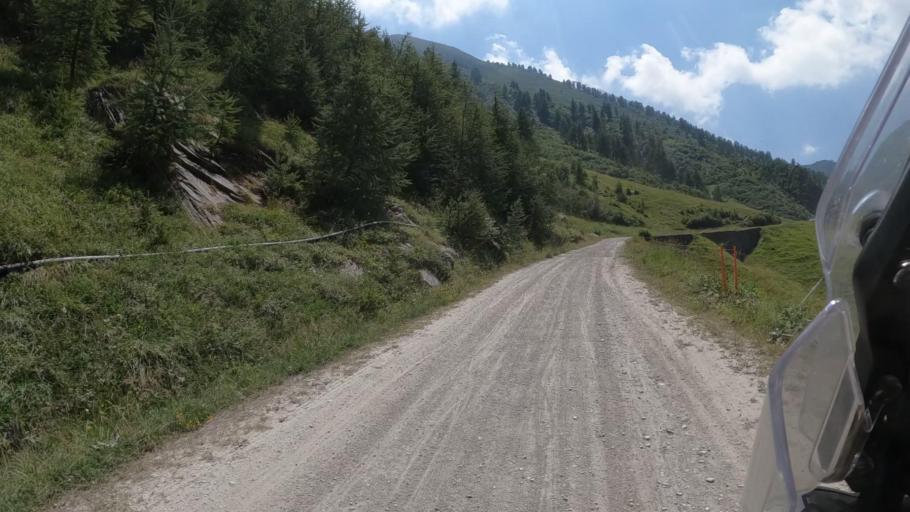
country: IT
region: Piedmont
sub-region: Provincia di Torino
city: Meana di Susa
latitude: 45.0891
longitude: 7.0665
